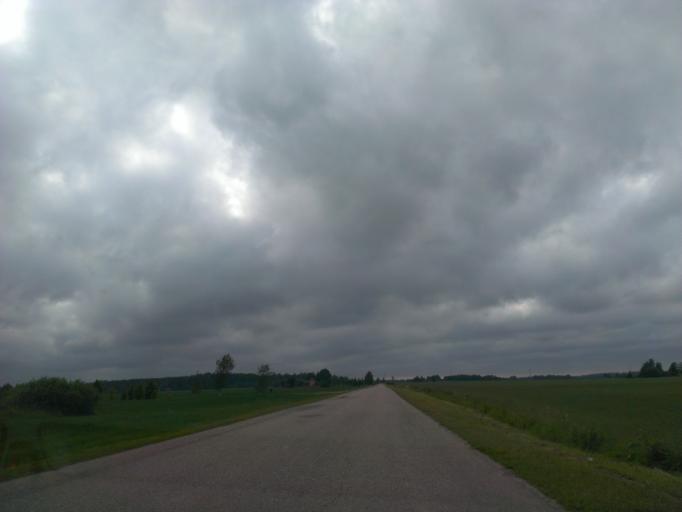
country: LV
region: Aizpute
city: Aizpute
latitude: 56.7149
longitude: 21.4661
